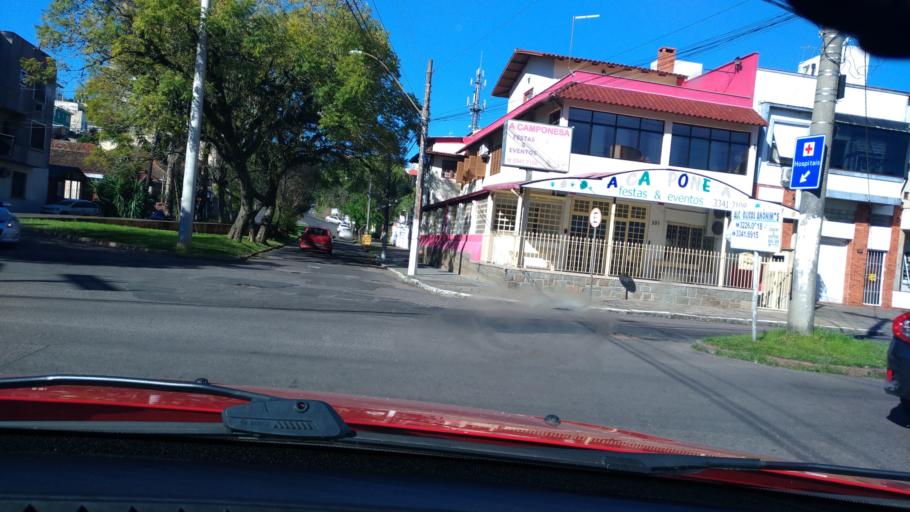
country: BR
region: Rio Grande do Sul
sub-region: Porto Alegre
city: Porto Alegre
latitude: -30.0096
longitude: -51.1667
